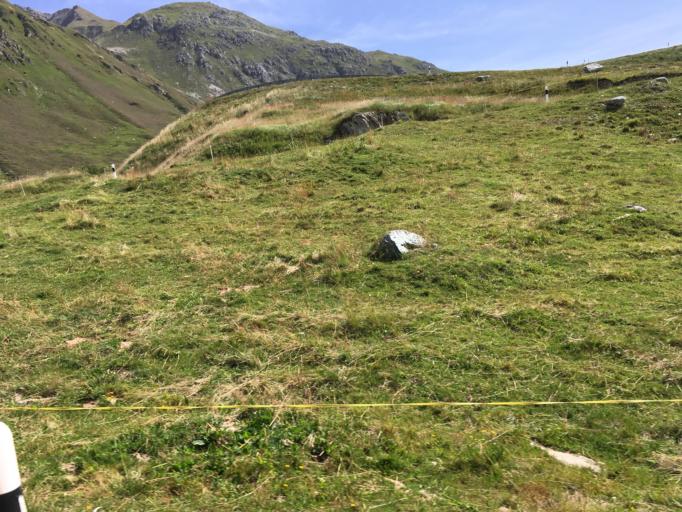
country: CH
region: Grisons
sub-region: Maloja District
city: Silvaplana
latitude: 46.4649
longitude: 9.6874
